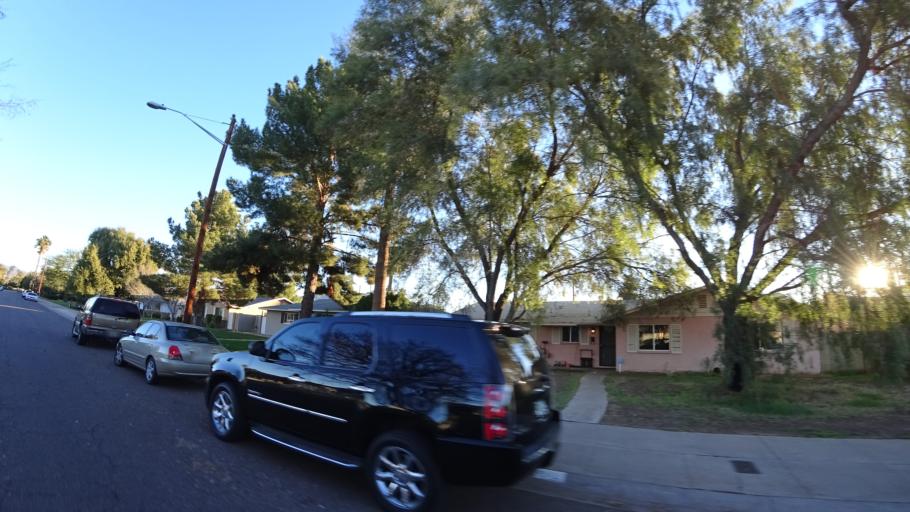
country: US
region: Arizona
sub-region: Maricopa County
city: Paradise Valley
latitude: 33.4848
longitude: -111.9924
